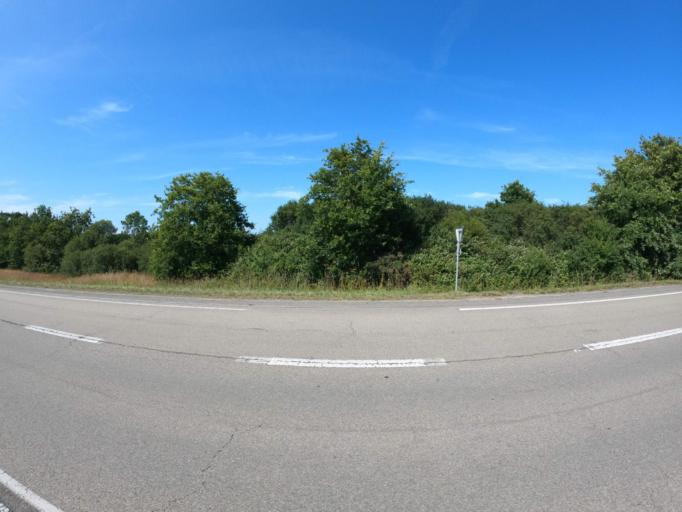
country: FR
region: Pays de la Loire
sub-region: Departement de la Loire-Atlantique
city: La Bernerie-en-Retz
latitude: 47.1057
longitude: -2.0539
